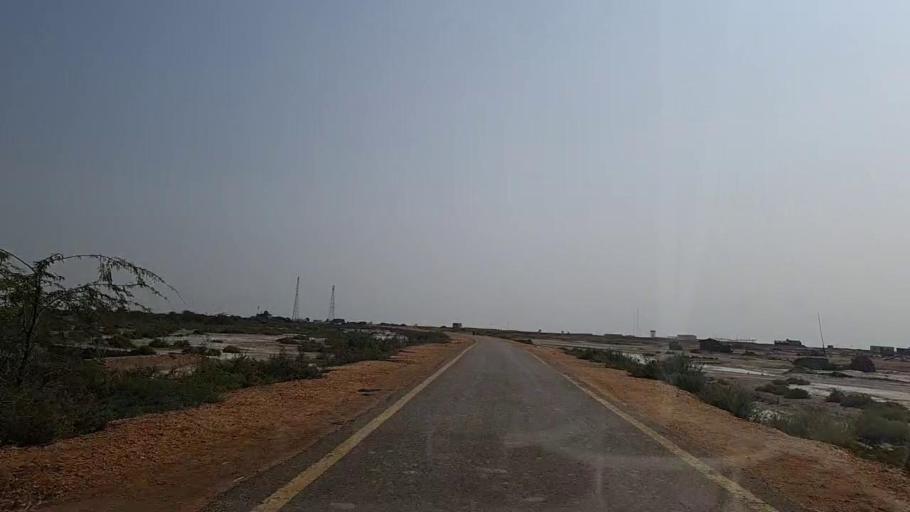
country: PK
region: Sindh
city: Chuhar Jamali
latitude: 24.1704
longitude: 67.8941
